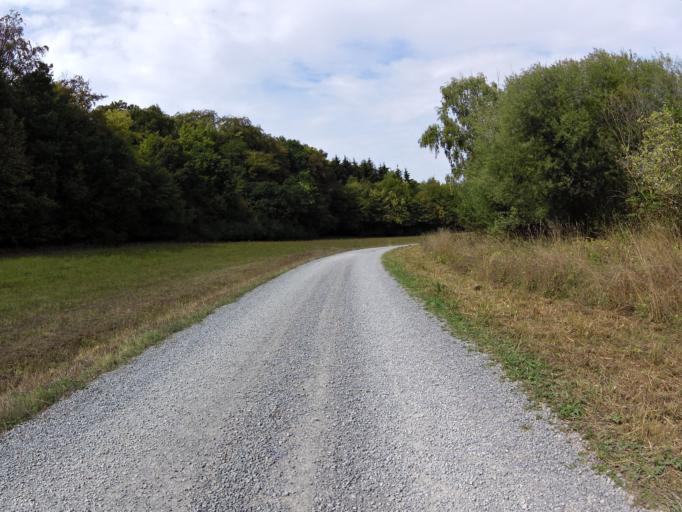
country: DE
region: Bavaria
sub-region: Regierungsbezirk Unterfranken
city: Eisingen
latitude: 49.7758
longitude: 9.8261
